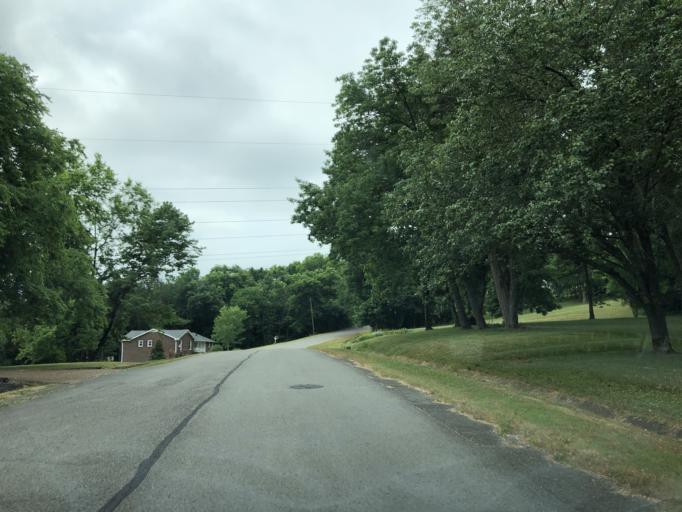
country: US
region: Tennessee
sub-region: Davidson County
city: Goodlettsville
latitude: 36.2878
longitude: -86.7343
